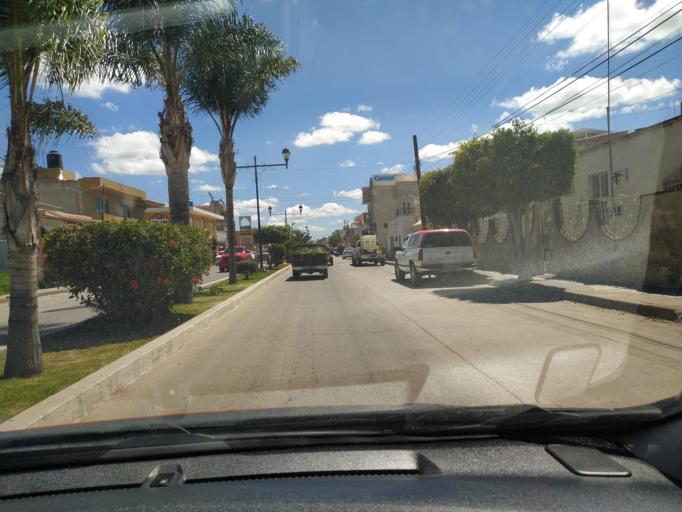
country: MX
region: Jalisco
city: San Julian
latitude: 21.0093
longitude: -102.1739
